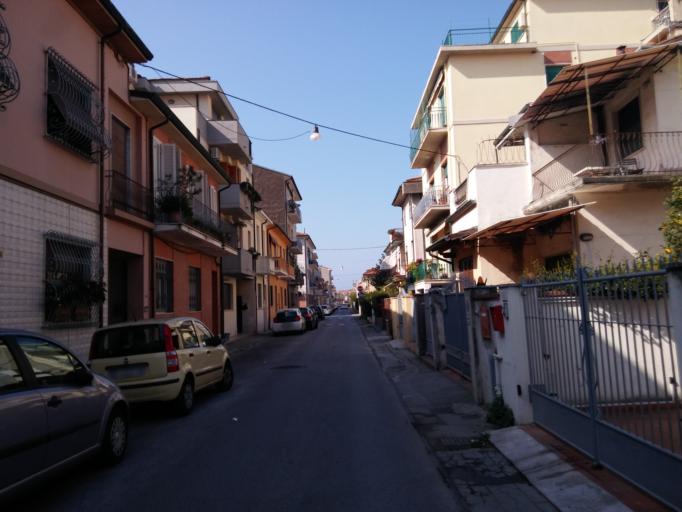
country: IT
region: Tuscany
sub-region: Provincia di Lucca
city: Viareggio
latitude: 43.8757
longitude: 10.2505
